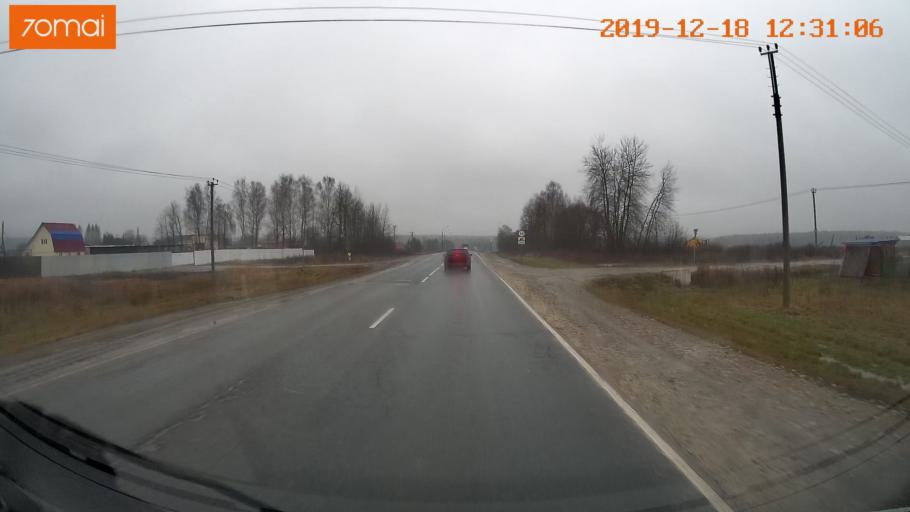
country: RU
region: Moskovskaya
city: Novopetrovskoye
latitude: 56.0970
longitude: 36.5397
